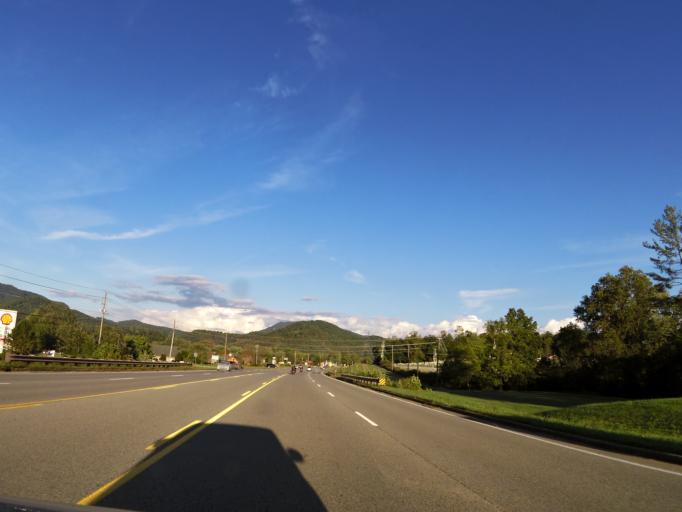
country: US
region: Tennessee
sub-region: Blount County
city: Wildwood
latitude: 35.6785
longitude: -83.7426
